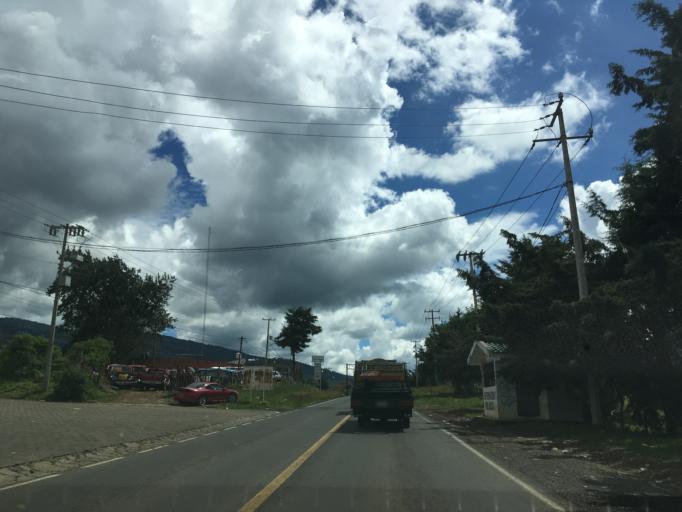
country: MX
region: Michoacan
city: Nahuatzen
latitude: 19.6581
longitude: -101.9288
